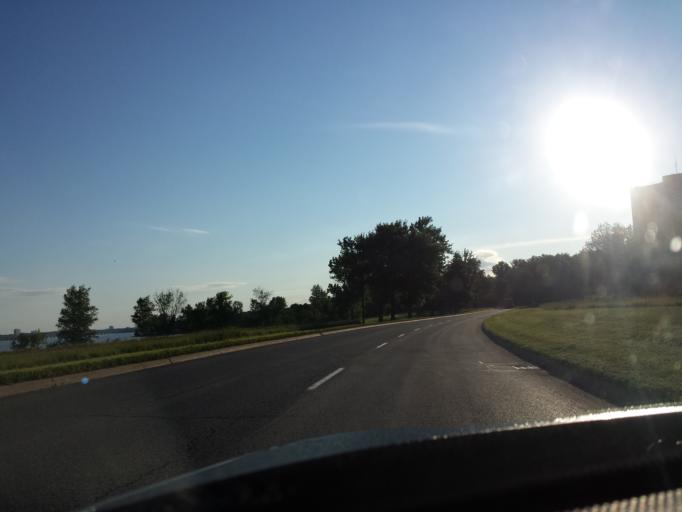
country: CA
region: Ontario
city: Bells Corners
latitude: 45.3745
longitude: -75.7839
